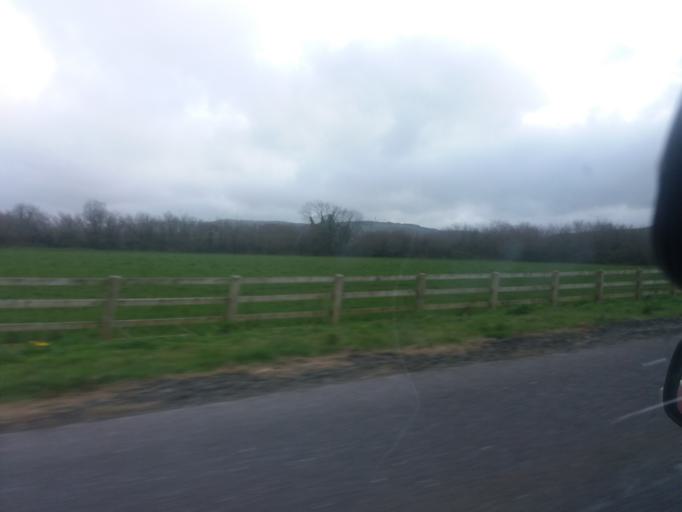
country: IE
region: Munster
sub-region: County Limerick
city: Newcastle West
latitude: 52.4357
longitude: -9.1068
